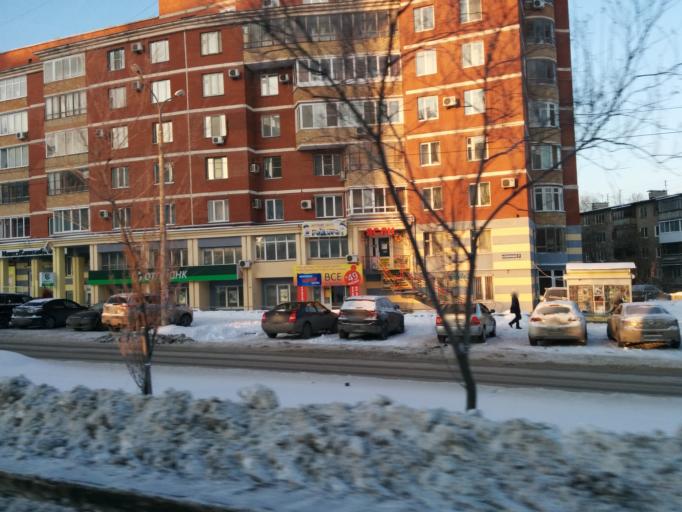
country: RU
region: Perm
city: Perm
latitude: 58.0060
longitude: 56.2714
